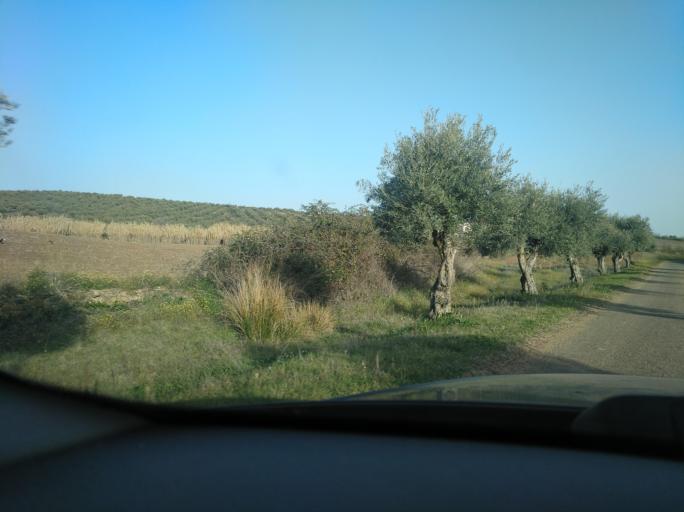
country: PT
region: Portalegre
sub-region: Campo Maior
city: Campo Maior
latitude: 39.0060
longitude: -7.0187
